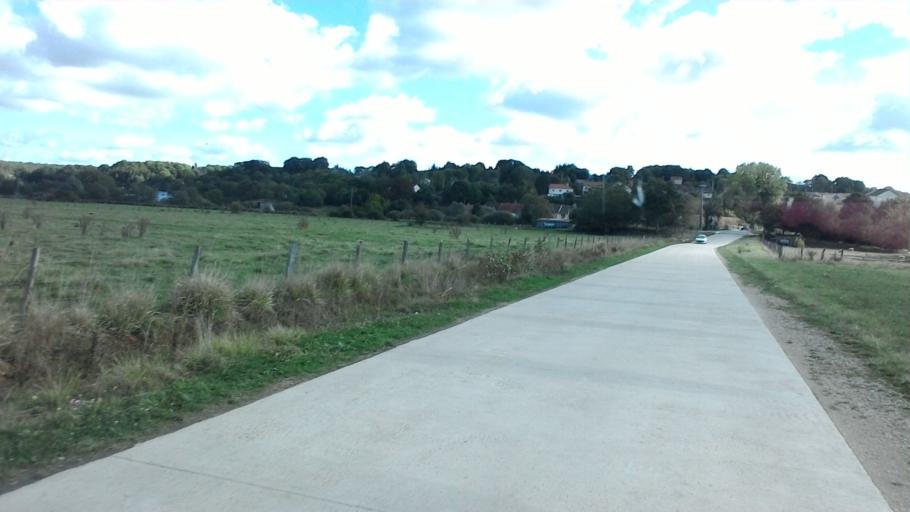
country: FR
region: Lorraine
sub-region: Departement des Vosges
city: Neufchateau
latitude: 48.3682
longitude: 5.6852
